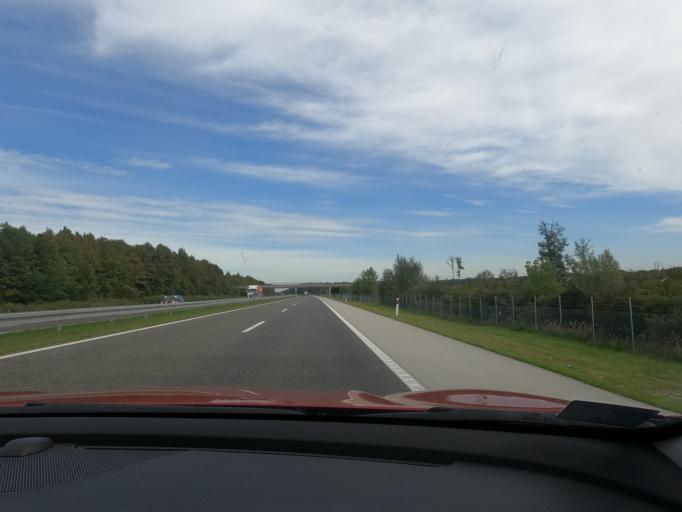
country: HR
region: Vukovarsko-Srijemska
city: Vrbanja
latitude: 45.0450
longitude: 18.9404
